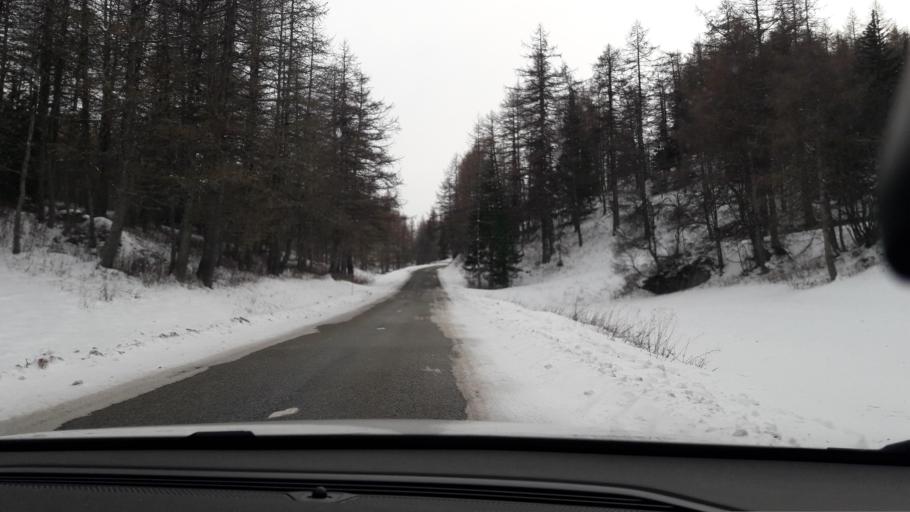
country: FR
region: Rhone-Alpes
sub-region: Departement de la Savoie
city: Saint-Michel-de-Maurienne
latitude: 45.2169
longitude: 6.4238
